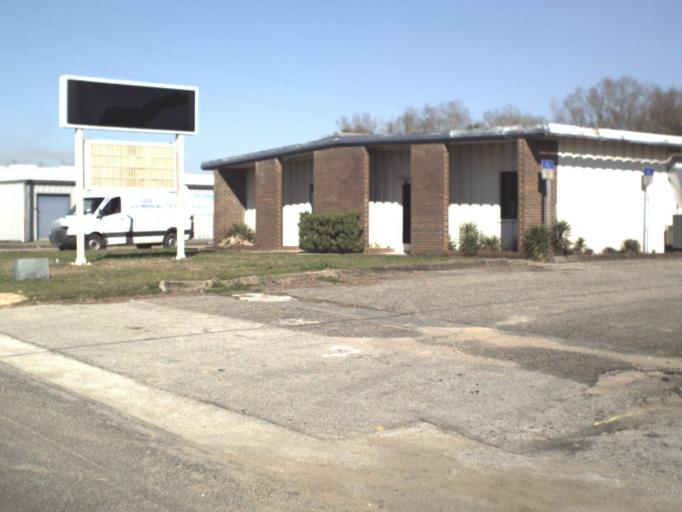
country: US
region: Florida
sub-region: Jackson County
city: Marianna
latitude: 30.7811
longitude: -85.2507
